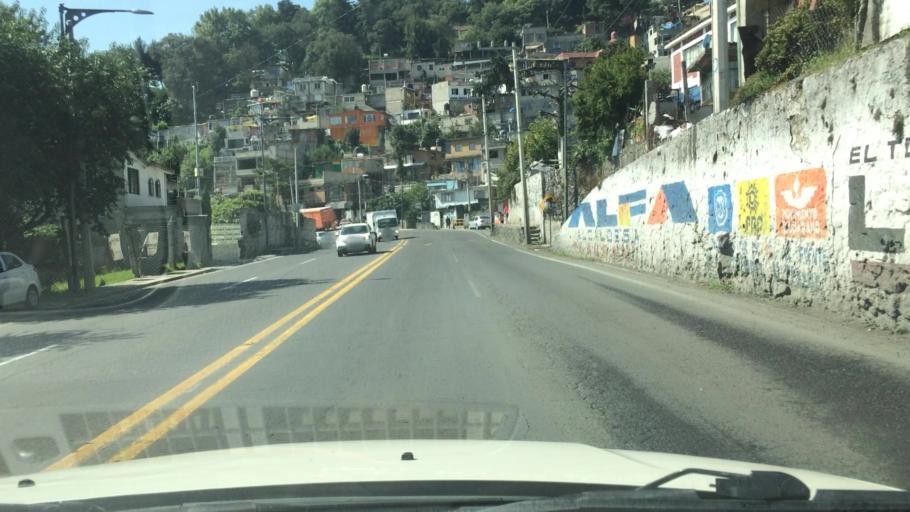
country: MX
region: Mexico City
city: Tlalpan
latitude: 19.2515
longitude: -99.1769
